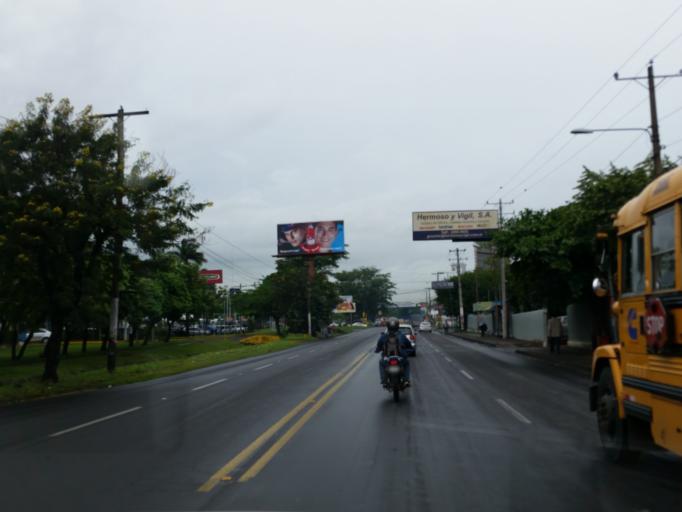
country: NI
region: Managua
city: Managua
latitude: 12.1426
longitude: -86.2937
